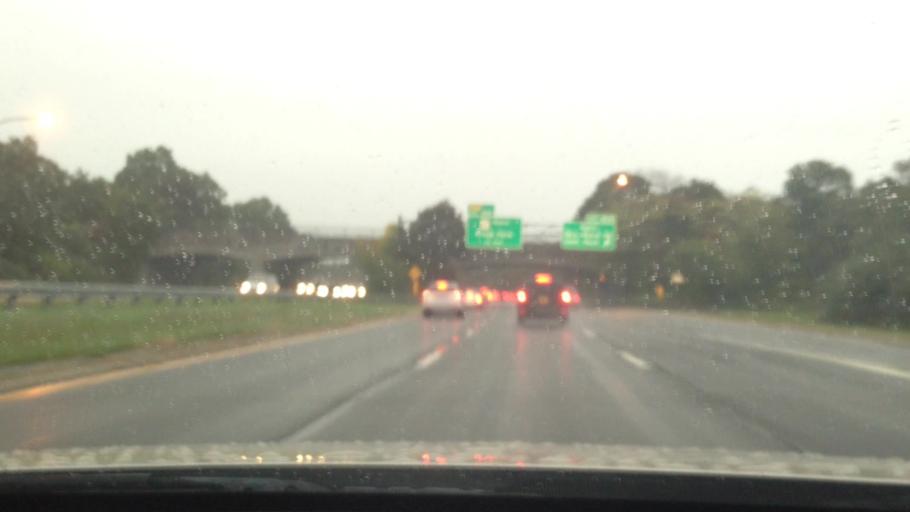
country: US
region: New York
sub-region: Suffolk County
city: Bay Wood
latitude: 40.7368
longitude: -73.2859
